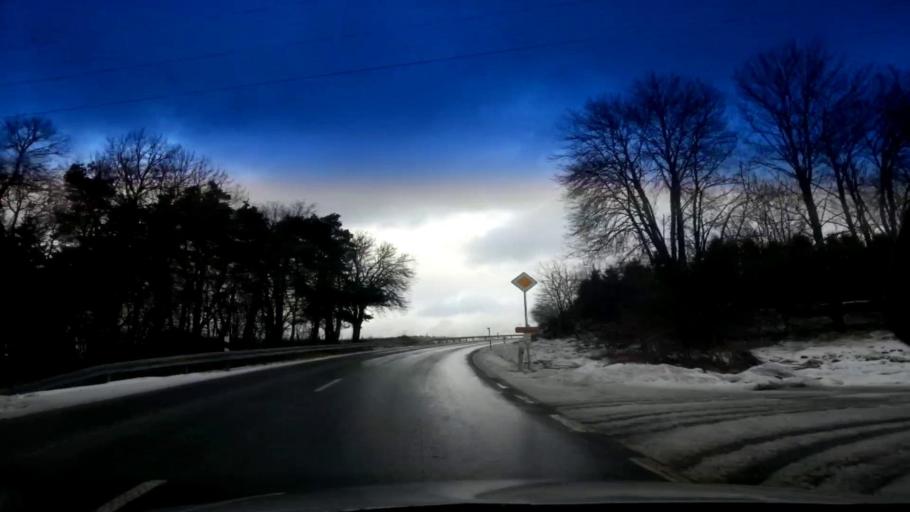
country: DE
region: Bavaria
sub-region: Upper Franconia
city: Weissenstadt
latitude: 50.1083
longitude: 11.8913
